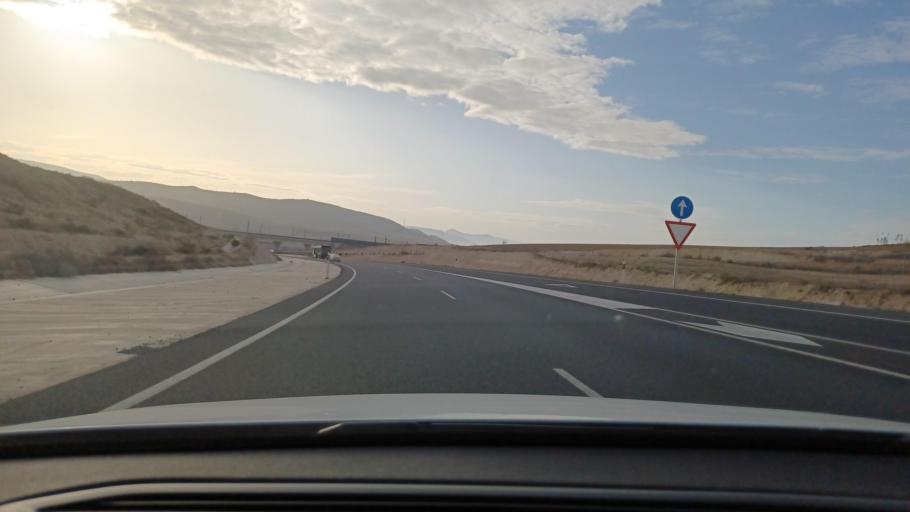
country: ES
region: Castille-La Mancha
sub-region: Provincia de Albacete
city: Caudete
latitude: 38.7219
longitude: -0.9371
